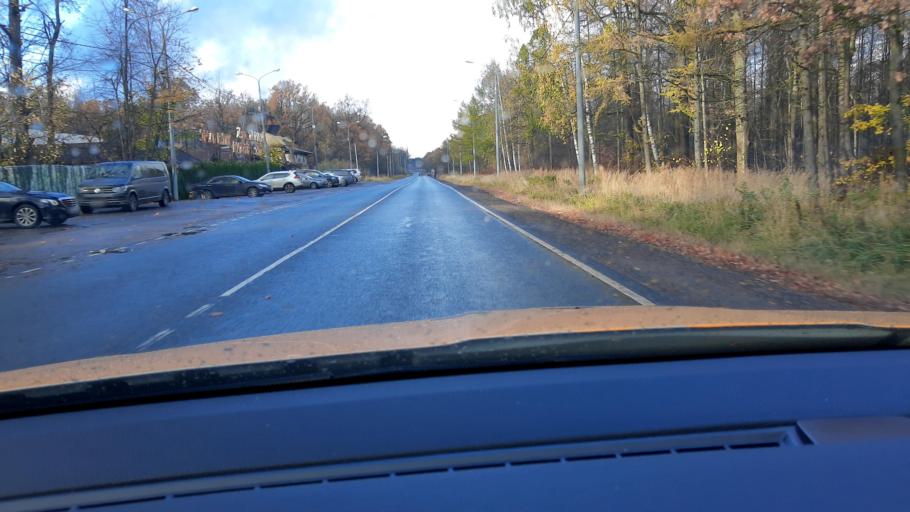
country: RU
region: Moskovskaya
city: Odintsovo
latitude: 55.6832
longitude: 37.2753
